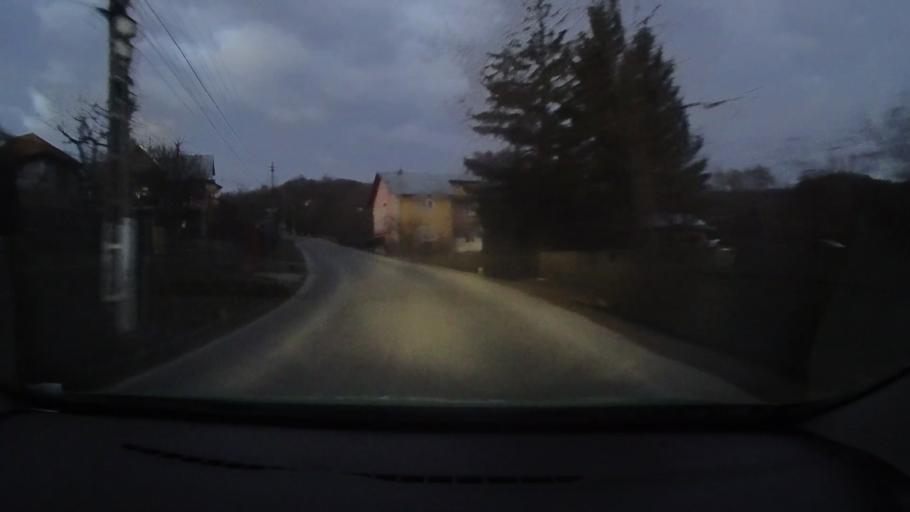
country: RO
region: Prahova
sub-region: Comuna Poiana Campina
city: Poiana Campina
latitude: 45.1251
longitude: 25.6773
